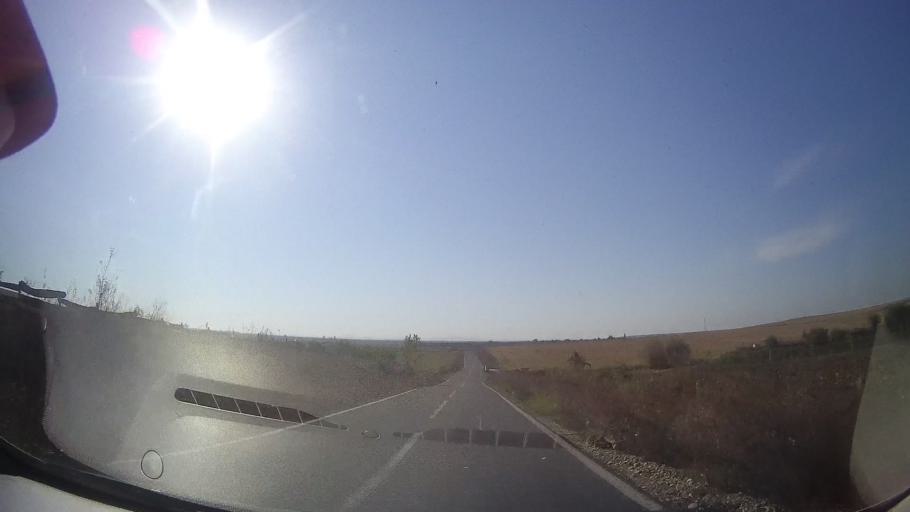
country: RO
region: Timis
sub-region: Comuna Topolovatu Mare
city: Topolovatu Mare
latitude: 45.8022
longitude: 21.5856
